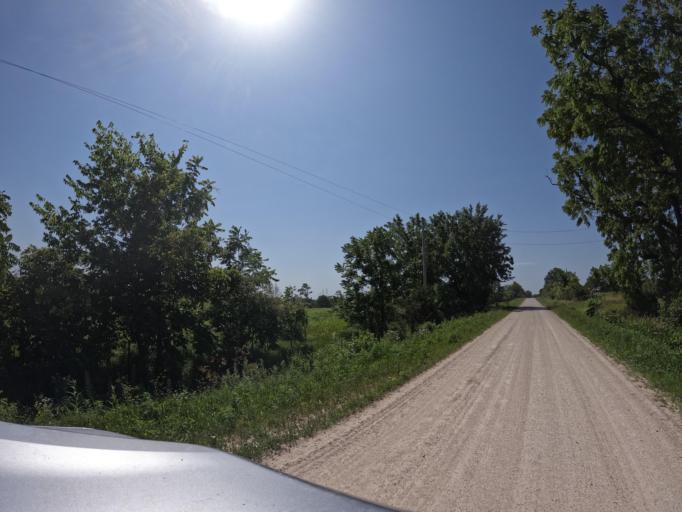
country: US
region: Iowa
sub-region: Henry County
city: Mount Pleasant
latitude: 40.9371
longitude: -91.5382
